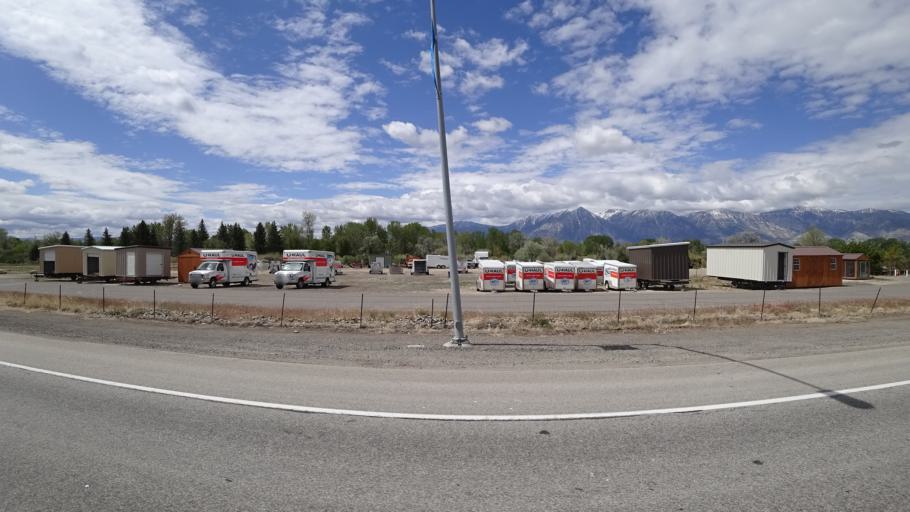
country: US
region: Nevada
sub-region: Douglas County
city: Gardnerville
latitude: 38.9194
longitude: -119.7211
